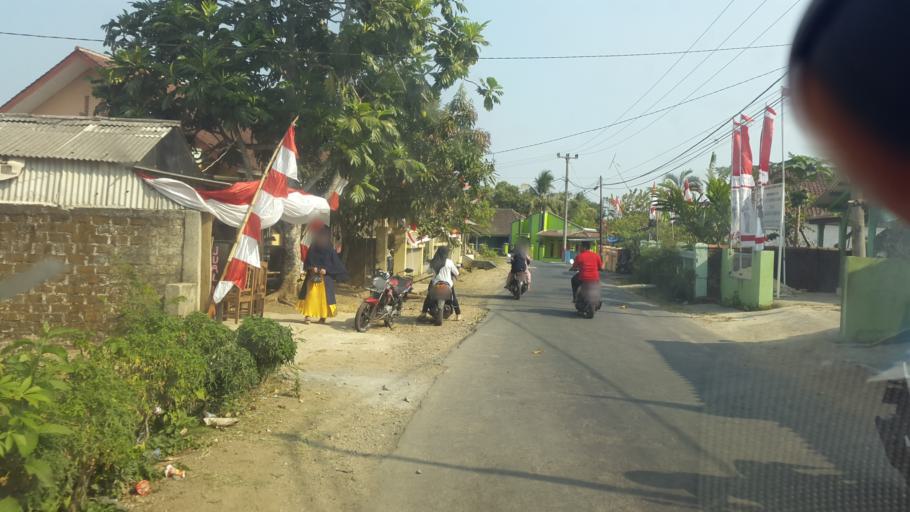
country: ID
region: West Java
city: Babakan Baru
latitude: -7.3217
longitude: 106.6209
